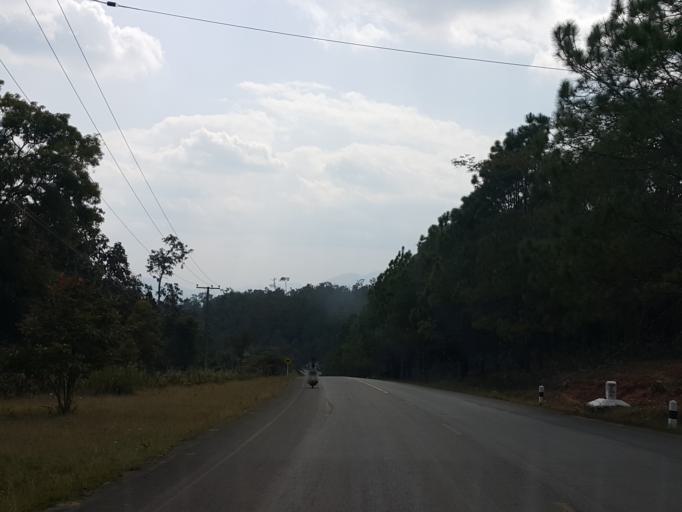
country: TH
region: Chiang Mai
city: Om Koi
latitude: 17.8552
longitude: 98.3715
